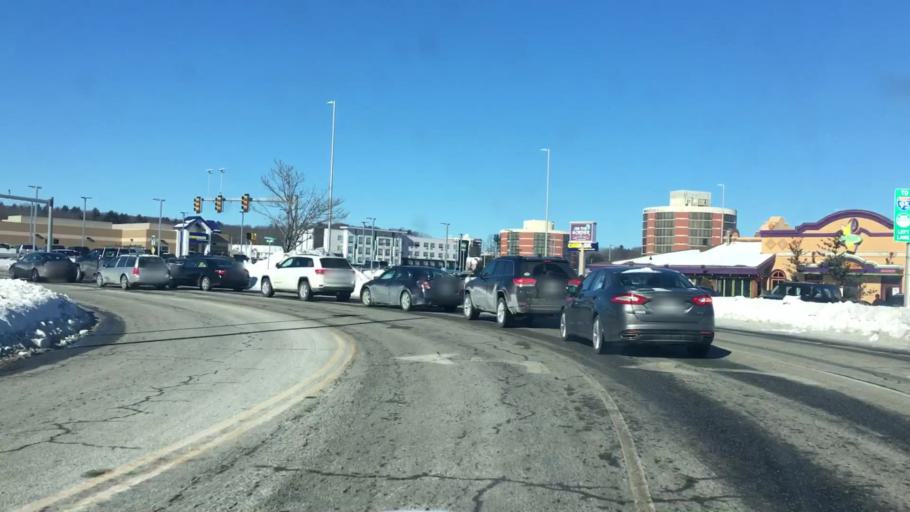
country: US
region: Maine
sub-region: Cumberland County
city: South Portland Gardens
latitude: 43.6324
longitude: -70.3386
